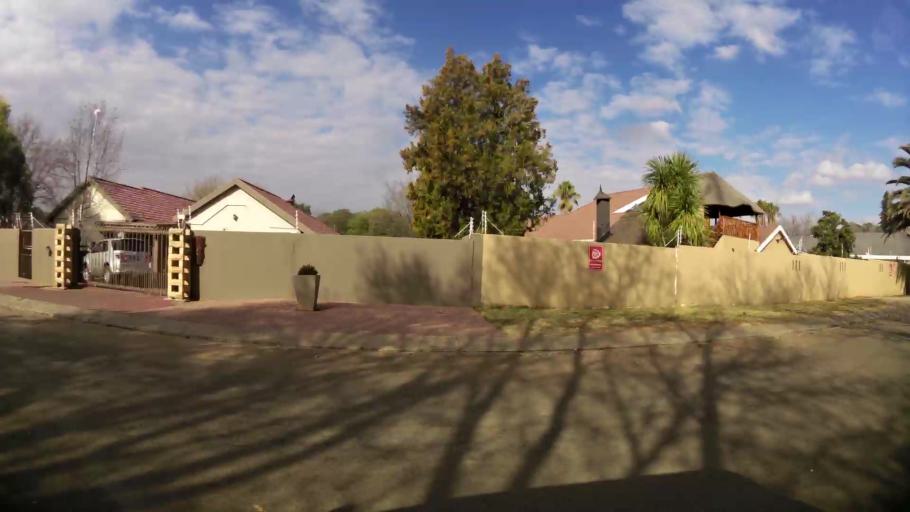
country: ZA
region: Orange Free State
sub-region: Mangaung Metropolitan Municipality
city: Bloemfontein
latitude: -29.0766
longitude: 26.2385
